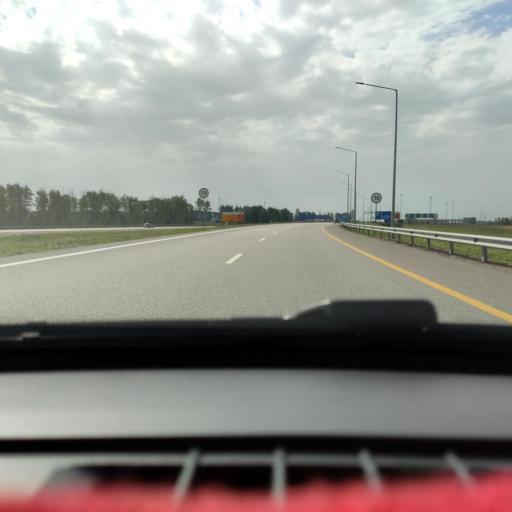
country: RU
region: Voronezj
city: Kashirskoye
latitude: 51.4780
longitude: 39.5519
